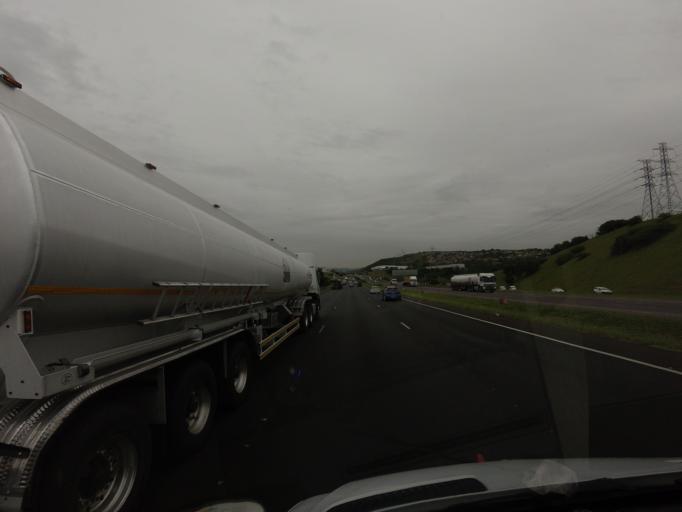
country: ZA
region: KwaZulu-Natal
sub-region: eThekwini Metropolitan Municipality
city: Berea
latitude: -29.7556
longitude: 31.0188
